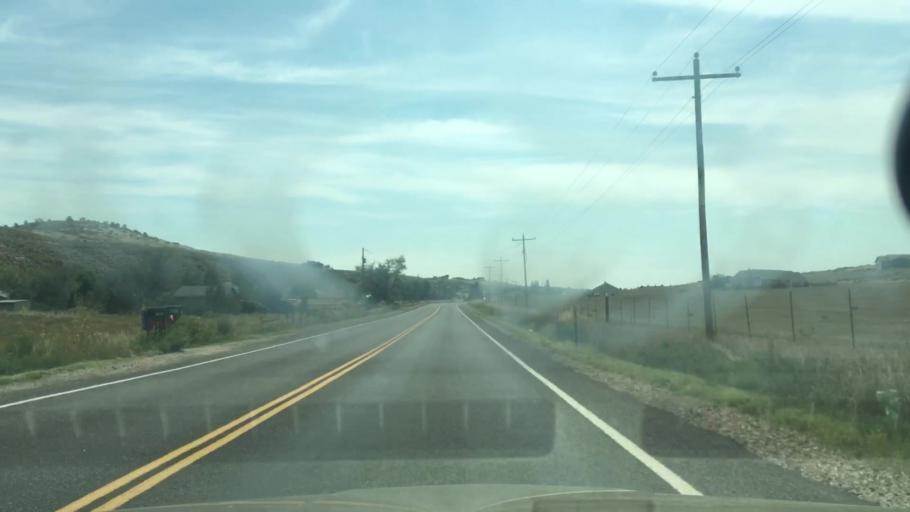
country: US
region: Colorado
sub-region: Larimer County
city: Campion
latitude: 40.3625
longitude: -105.1877
